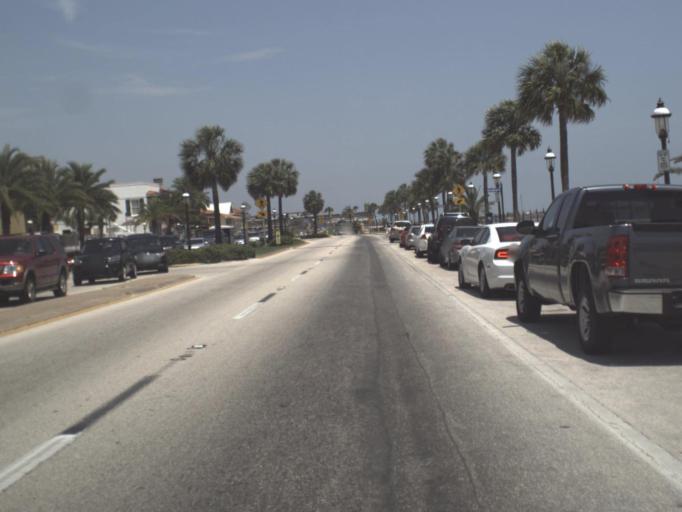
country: US
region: Florida
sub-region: Saint Johns County
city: Saint Augustine
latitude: 29.8936
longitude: -81.3109
